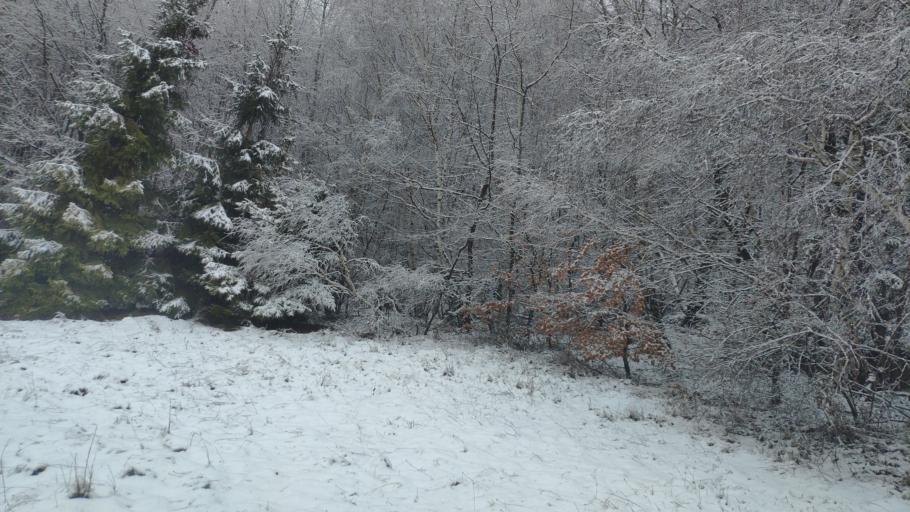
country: SK
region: Kosicky
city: Moldava nad Bodvou
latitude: 48.7404
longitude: 21.0875
